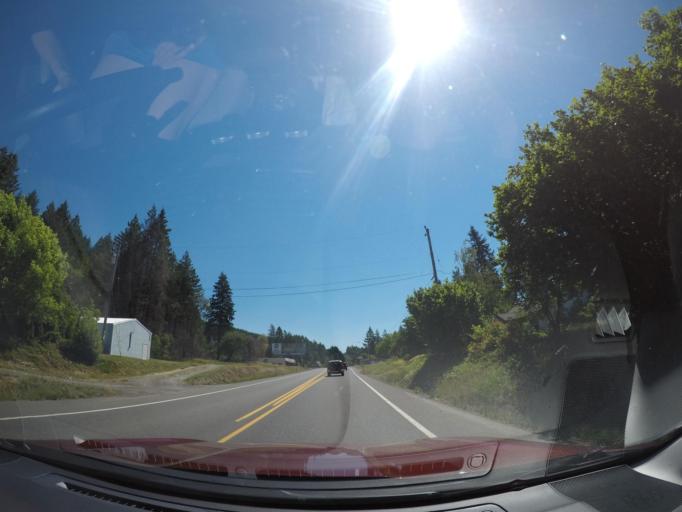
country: US
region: Oregon
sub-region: Linn County
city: Mill City
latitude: 44.7574
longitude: -122.4893
